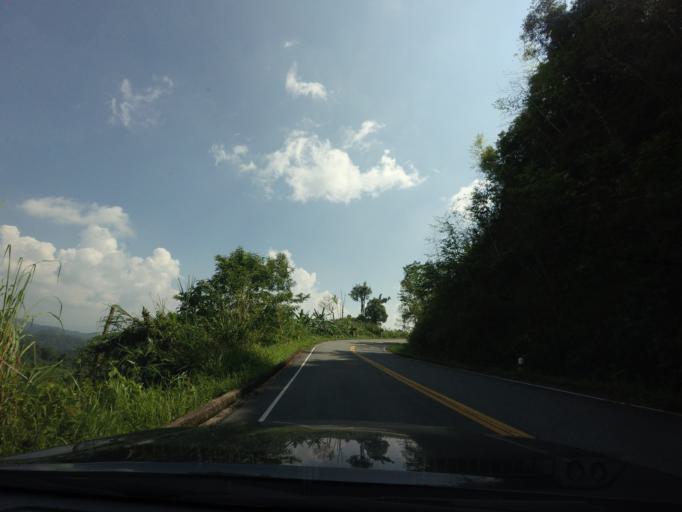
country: TH
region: Nan
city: Bo Kluea
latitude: 19.0583
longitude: 101.0913
